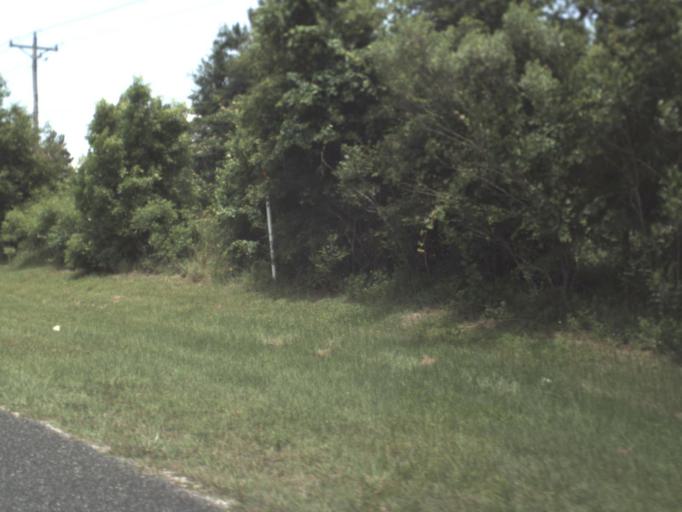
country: US
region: Florida
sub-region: Alachua County
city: Newberry
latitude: 29.6542
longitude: -82.5367
